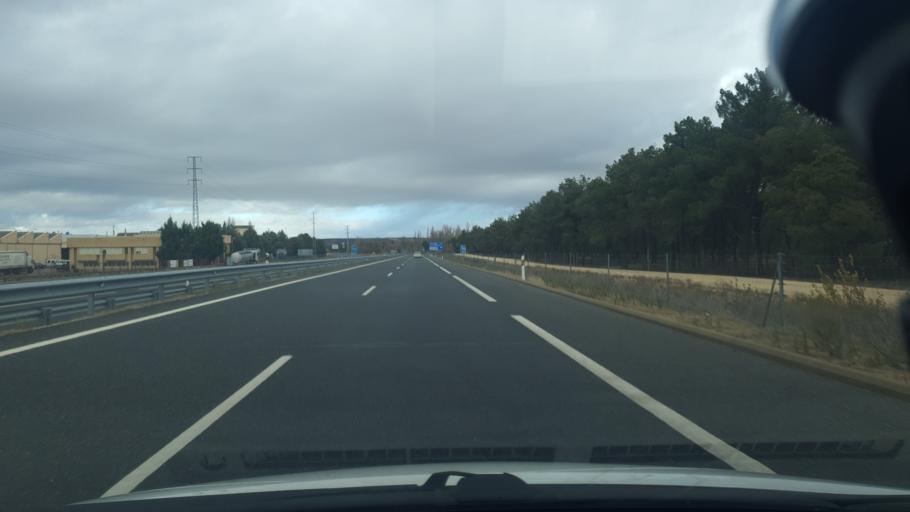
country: ES
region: Castille and Leon
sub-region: Provincia de Segovia
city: Sanchonuno
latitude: 41.3585
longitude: -4.2991
